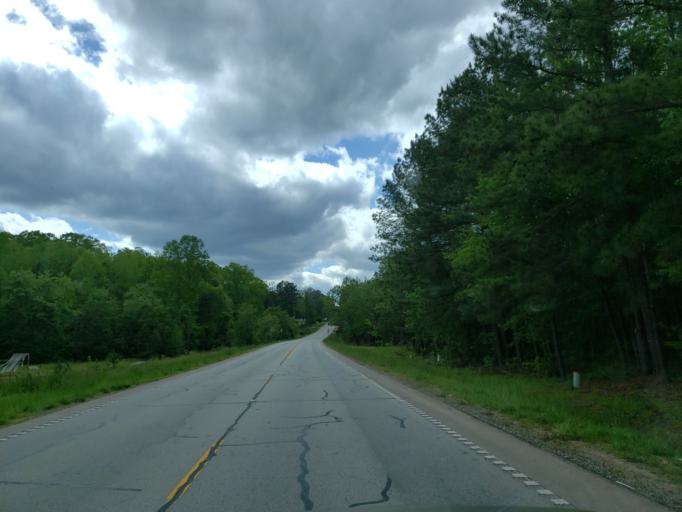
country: US
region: Georgia
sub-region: Haralson County
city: Tallapoosa
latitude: 33.7465
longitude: -85.3514
